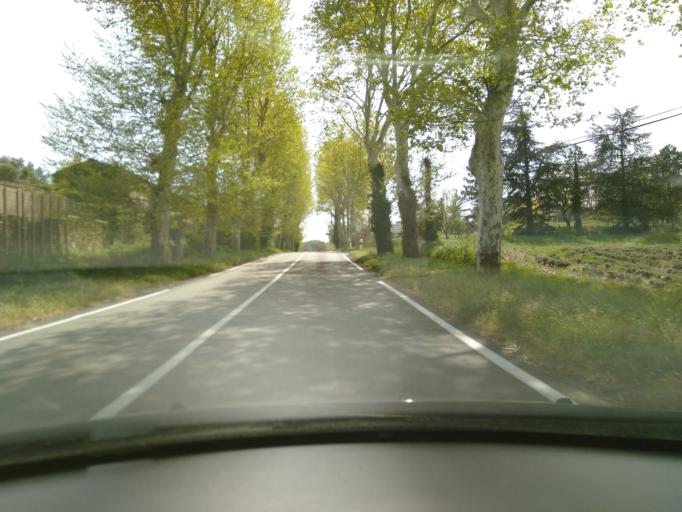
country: FR
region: Rhone-Alpes
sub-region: Departement de la Drome
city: Malataverne
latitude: 44.4958
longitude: 4.7431
